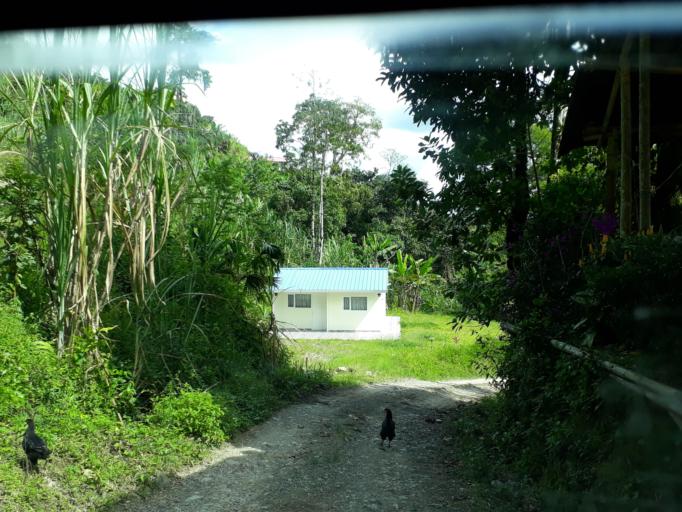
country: CO
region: Cundinamarca
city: Topaipi
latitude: 5.2781
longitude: -74.3507
